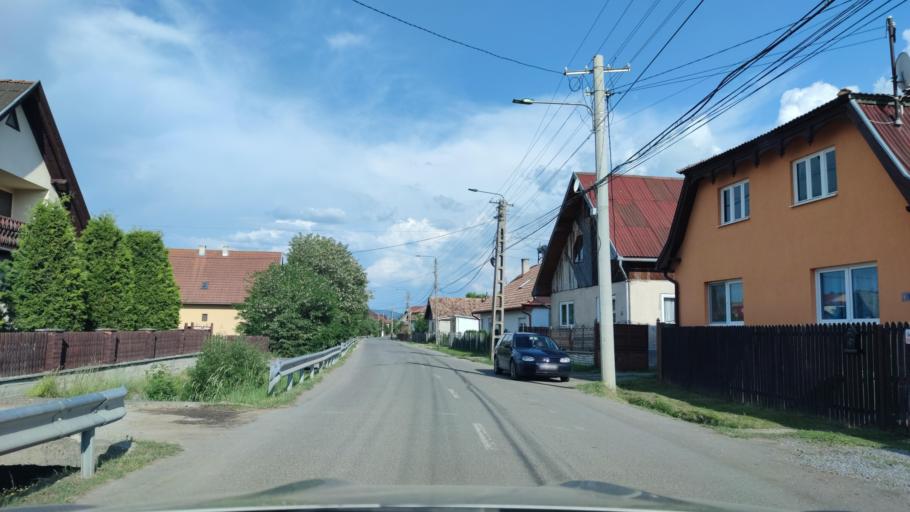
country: RO
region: Harghita
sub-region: Comuna Remetea
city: Remetea
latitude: 46.7953
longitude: 25.4351
